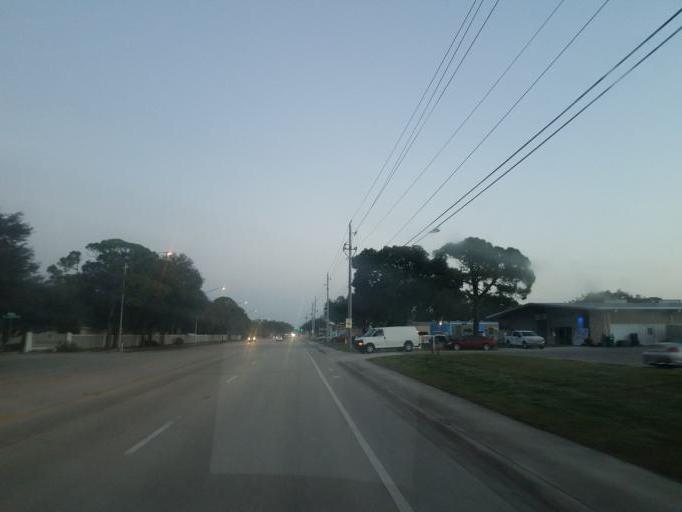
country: US
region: Florida
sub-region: Sarasota County
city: Fruitville
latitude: 27.3174
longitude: -82.4514
